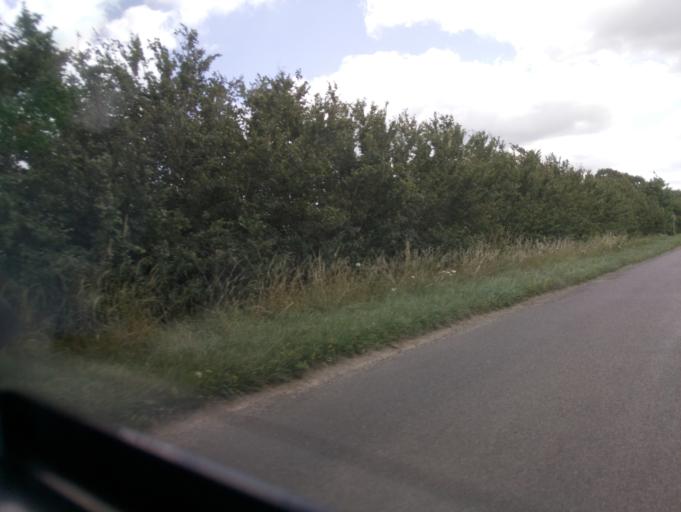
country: GB
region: England
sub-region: Oxfordshire
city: Faringdon
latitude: 51.6221
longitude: -1.6145
